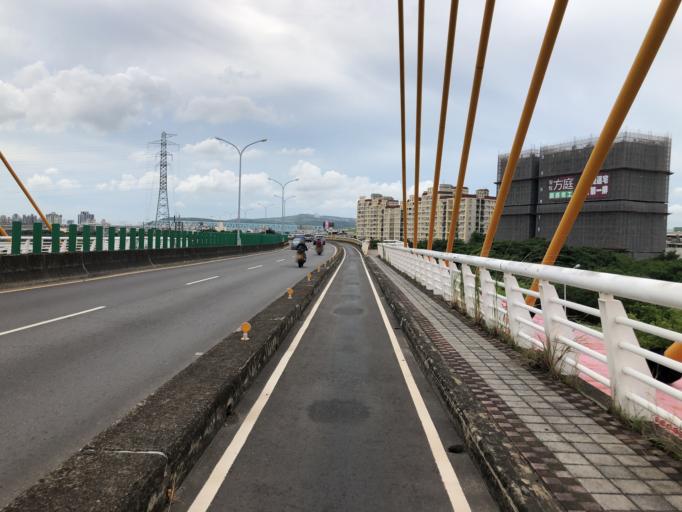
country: TW
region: Taiwan
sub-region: Changhua
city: Chang-hua
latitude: 24.0991
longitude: 120.6256
